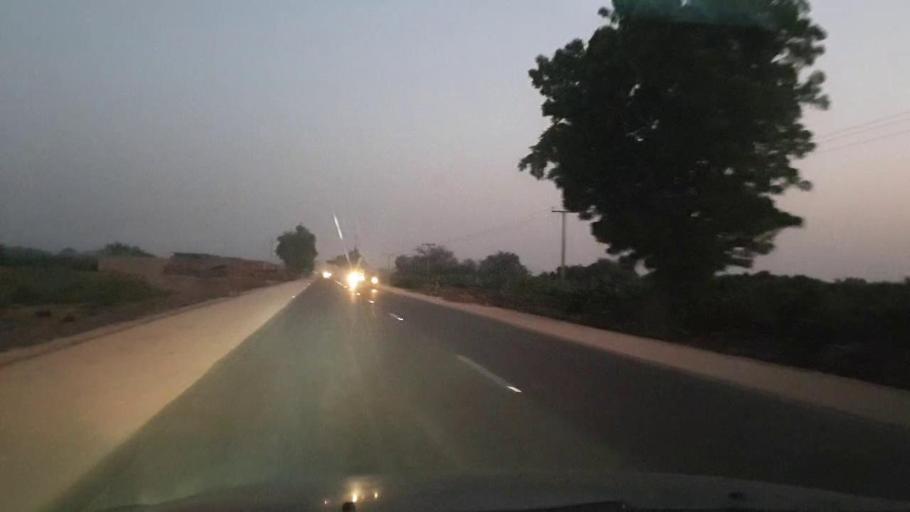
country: PK
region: Sindh
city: Tando Allahyar
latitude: 25.4023
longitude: 68.7618
